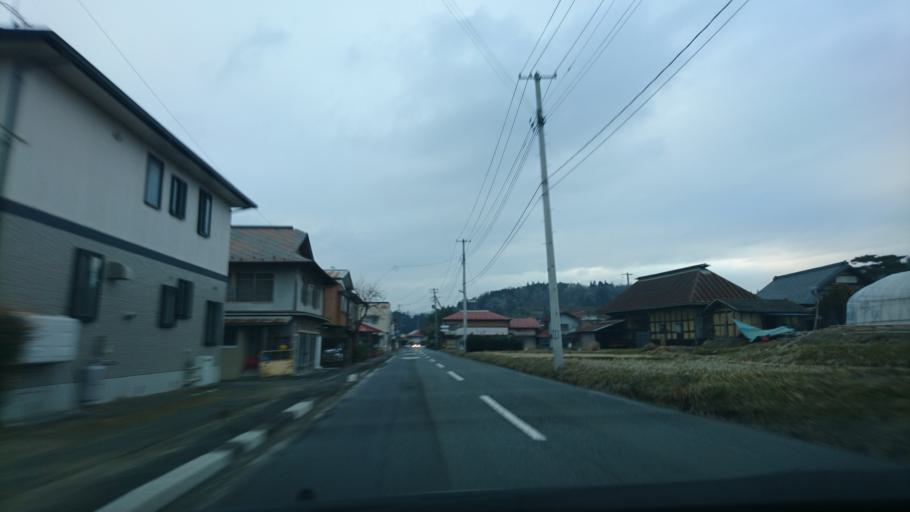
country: JP
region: Iwate
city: Ichinoseki
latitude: 39.0177
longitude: 141.3423
